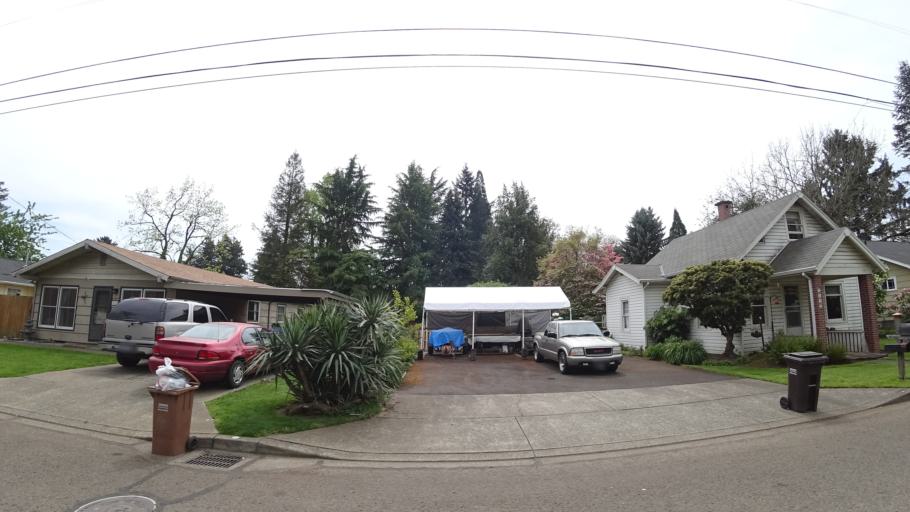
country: US
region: Oregon
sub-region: Clackamas County
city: Milwaukie
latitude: 45.4558
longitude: -122.6250
